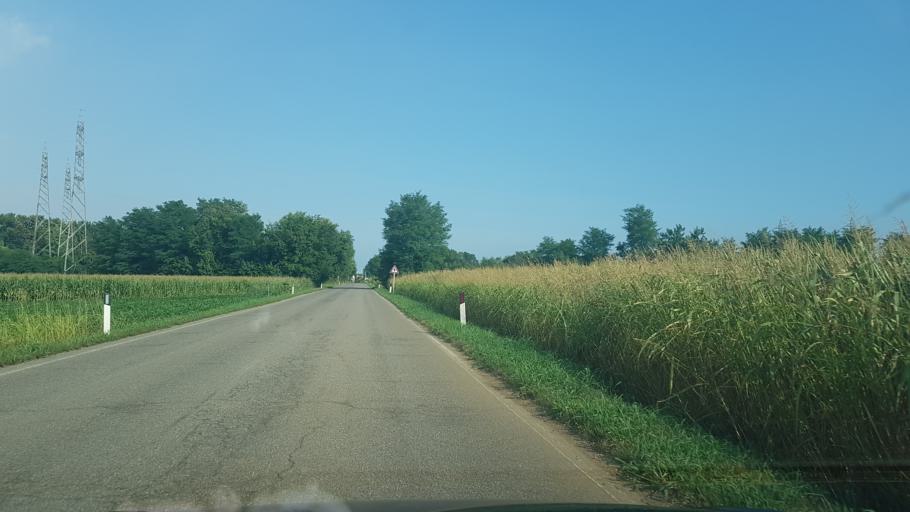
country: IT
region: Friuli Venezia Giulia
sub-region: Provincia di Udine
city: Colloredo di Prato
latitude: 46.0521
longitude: 13.1272
